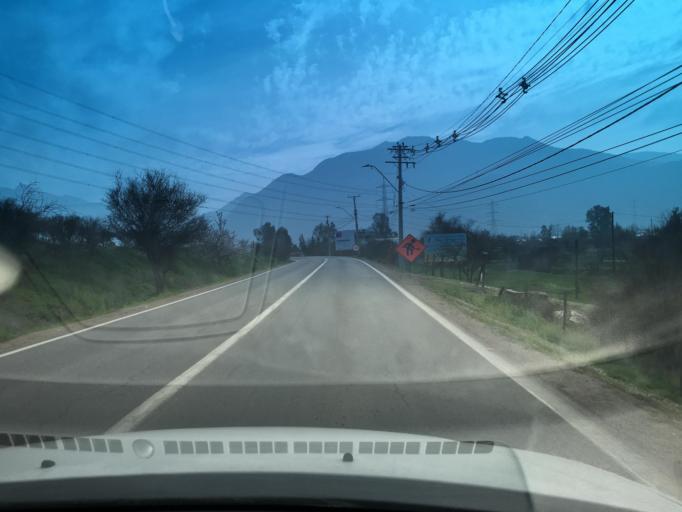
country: CL
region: Santiago Metropolitan
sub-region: Provincia de Chacabuco
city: Lampa
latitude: -33.2666
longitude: -70.8964
